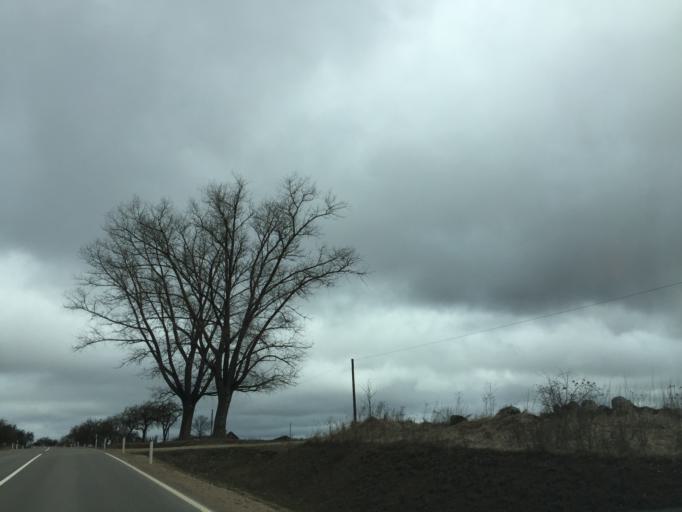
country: LV
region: Ilukste
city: Ilukste
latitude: 55.9905
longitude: 26.2892
